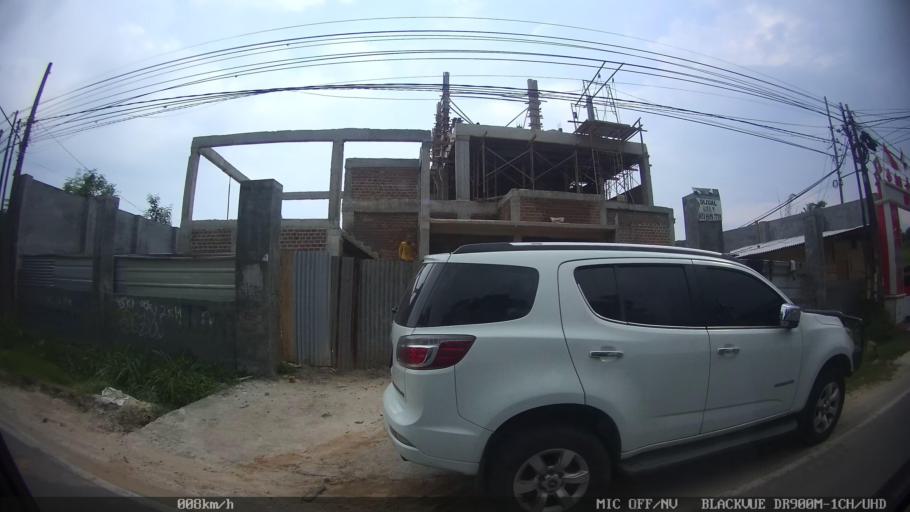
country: ID
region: Lampung
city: Bandarlampung
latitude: -5.4268
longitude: 105.2664
